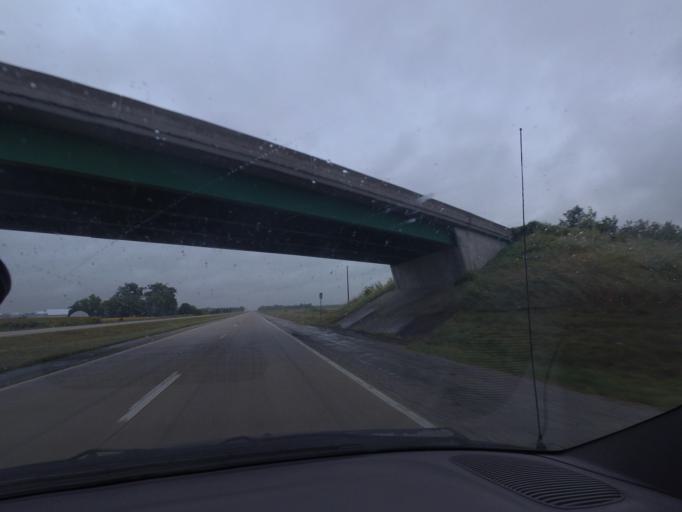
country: US
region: Illinois
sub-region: Adams County
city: Payson
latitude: 39.7435
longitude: -91.2661
